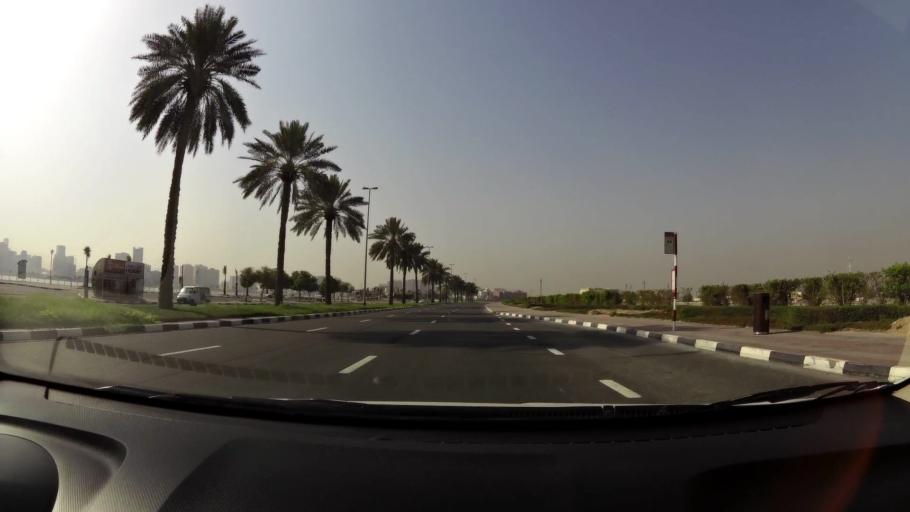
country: AE
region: Ash Shariqah
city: Sharjah
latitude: 25.3024
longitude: 55.3484
